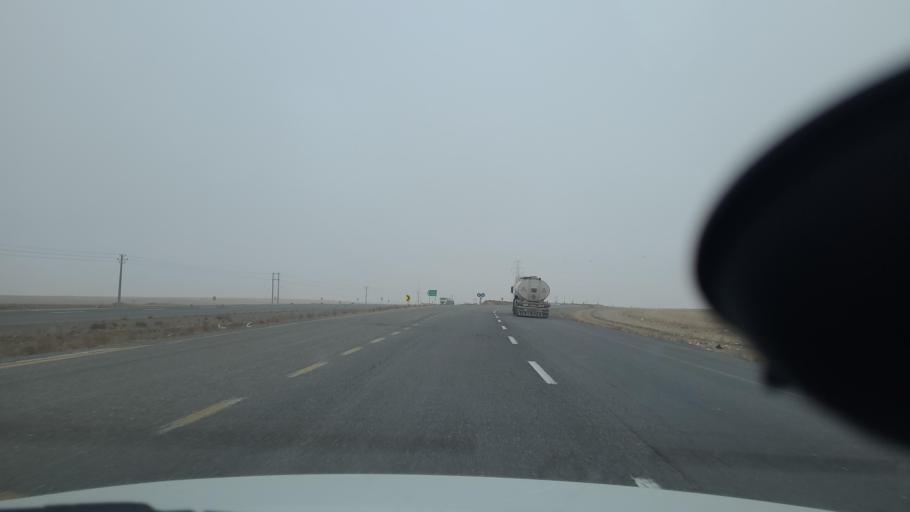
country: IR
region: Razavi Khorasan
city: Fariman
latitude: 35.8693
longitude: 59.7621
